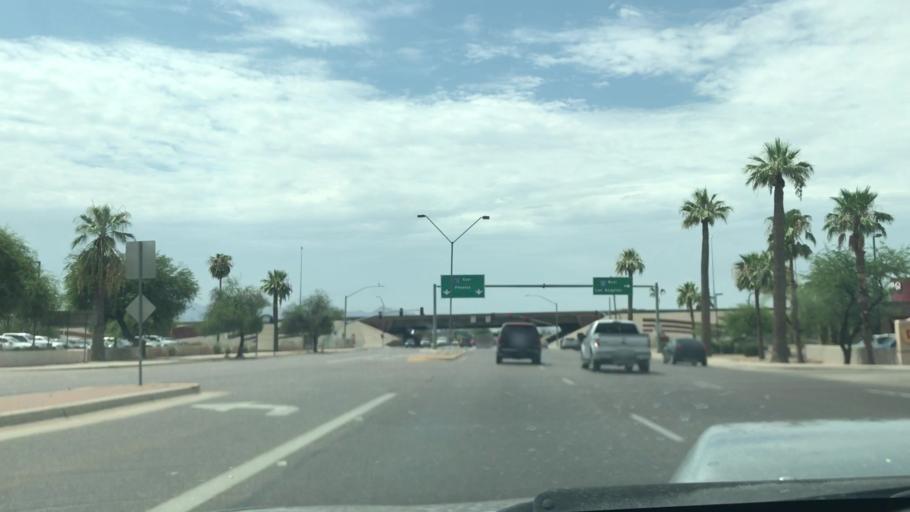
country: US
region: Arizona
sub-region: Maricopa County
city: Goodyear
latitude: 33.4602
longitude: -112.3582
